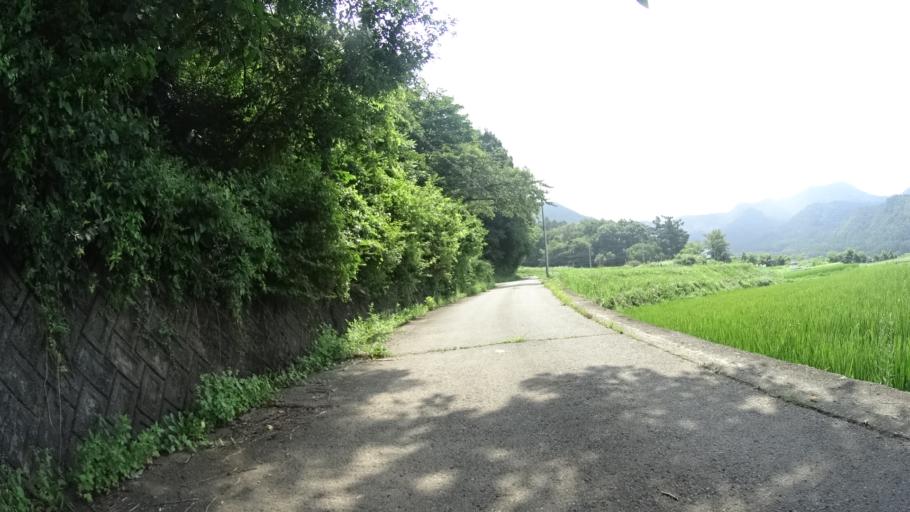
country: JP
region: Yamanashi
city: Nirasaki
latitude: 35.8927
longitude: 138.4720
